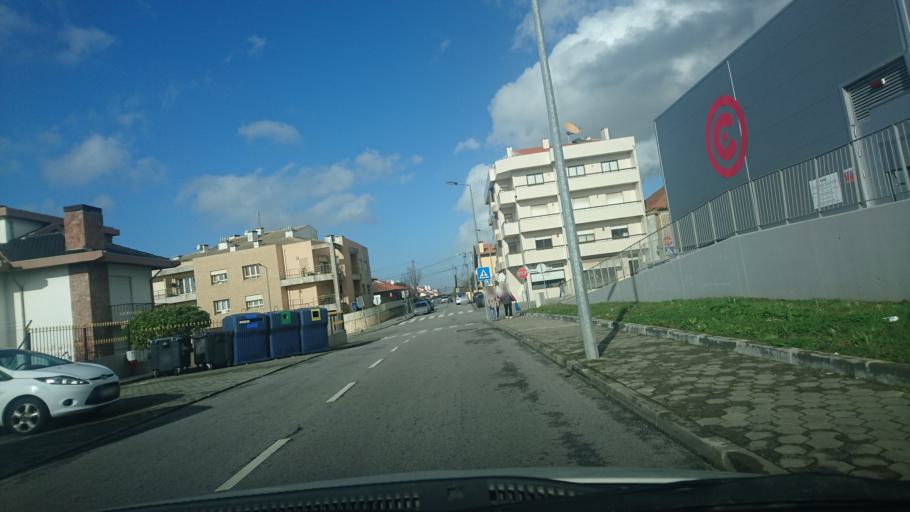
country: PT
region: Aveiro
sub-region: Ovar
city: Esmoriz
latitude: 40.9614
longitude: -8.6296
